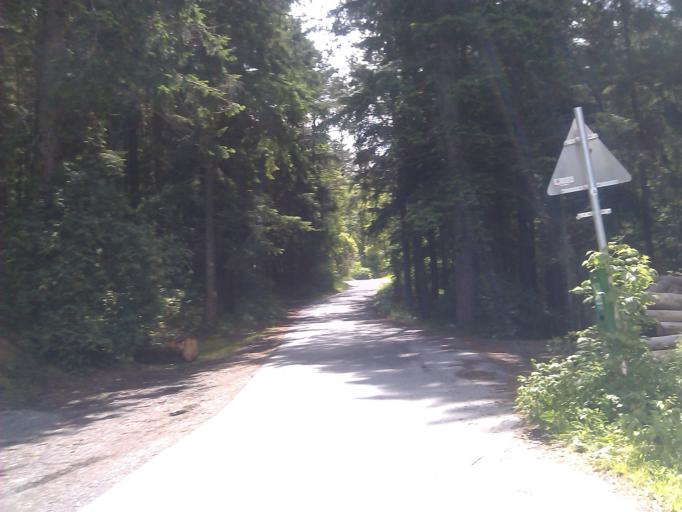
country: AT
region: Tyrol
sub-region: Politischer Bezirk Landeck
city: Pfunds
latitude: 46.9501
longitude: 10.5101
